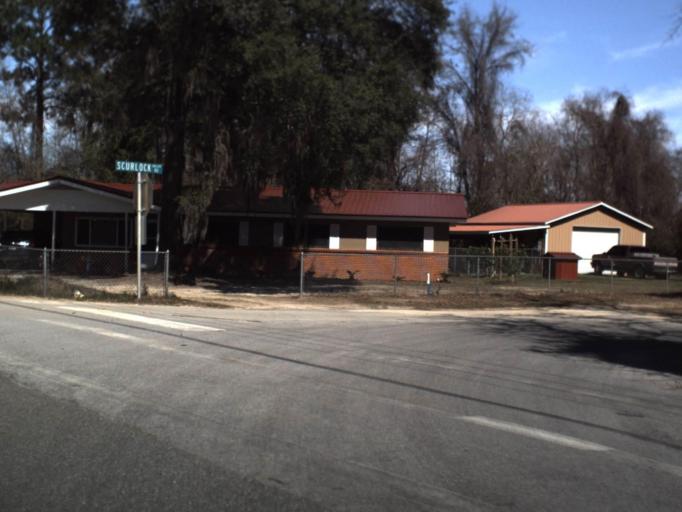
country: US
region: Florida
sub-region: Bay County
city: Lynn Haven
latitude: 30.2842
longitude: -85.6356
